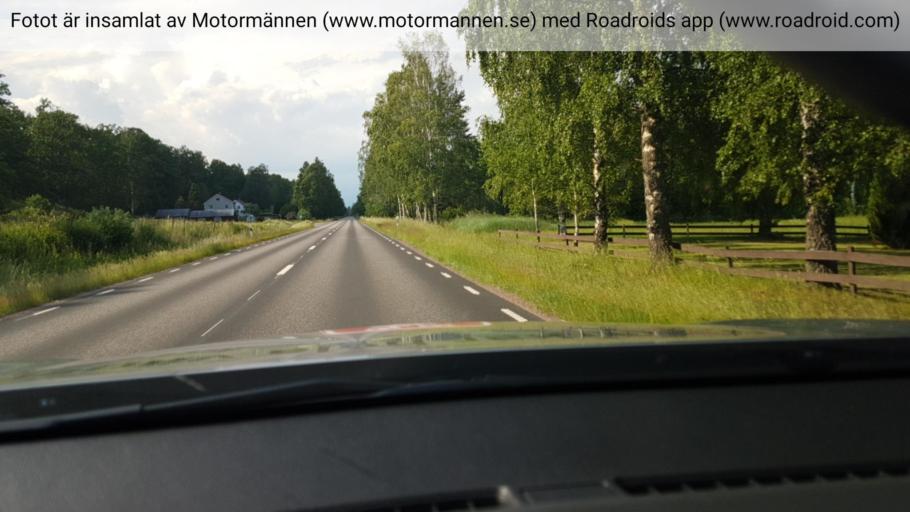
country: SE
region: Vaestra Goetaland
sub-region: Hjo Kommun
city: Hjo
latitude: 58.1523
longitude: 14.2140
